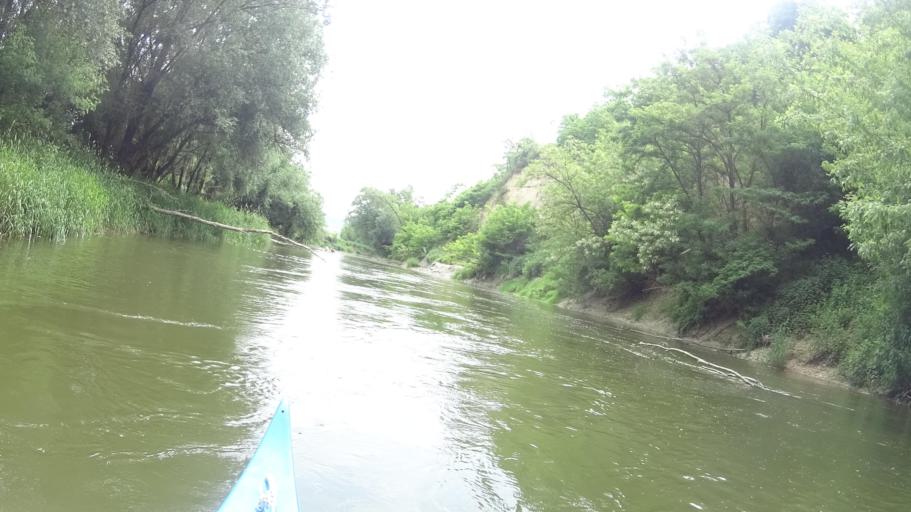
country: HU
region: Komarom-Esztergom
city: Esztergom
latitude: 47.9157
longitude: 18.7585
